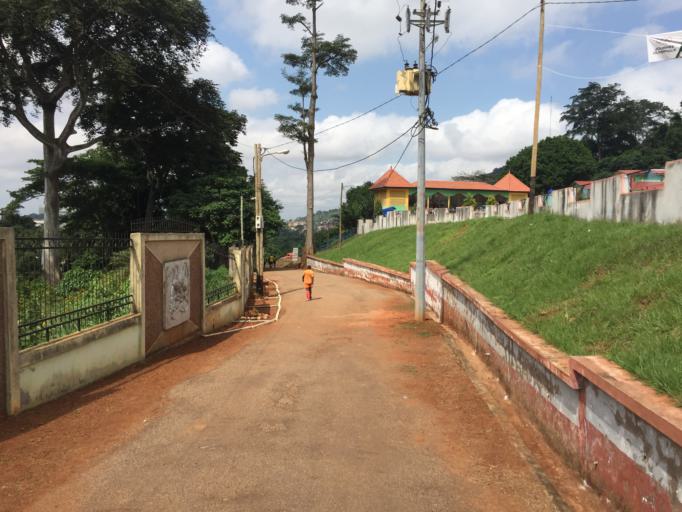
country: CM
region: Centre
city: Yaounde
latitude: 3.9143
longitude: 11.5004
